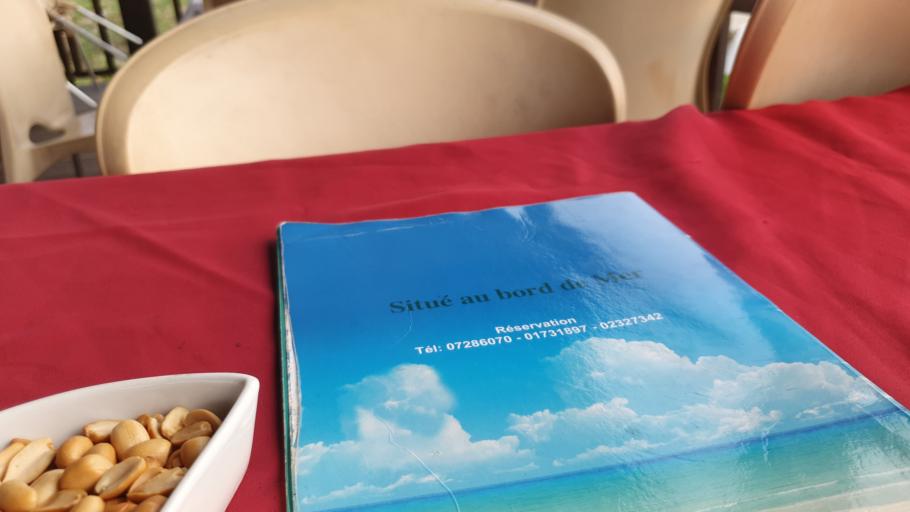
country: GA
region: Estuaire
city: Libreville
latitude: 0.4264
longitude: 9.4209
